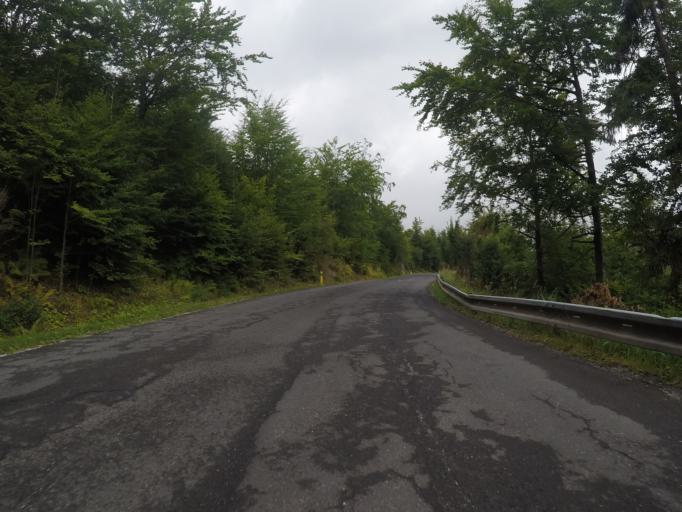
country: SK
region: Kosicky
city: Spisska Nova Ves
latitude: 48.8670
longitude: 20.5265
